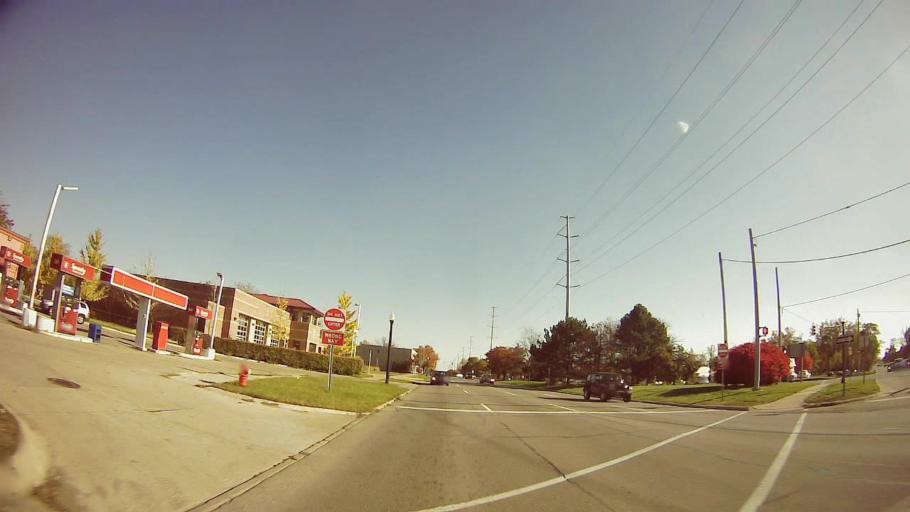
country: US
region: Michigan
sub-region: Oakland County
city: Farmington
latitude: 42.4484
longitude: -83.3365
